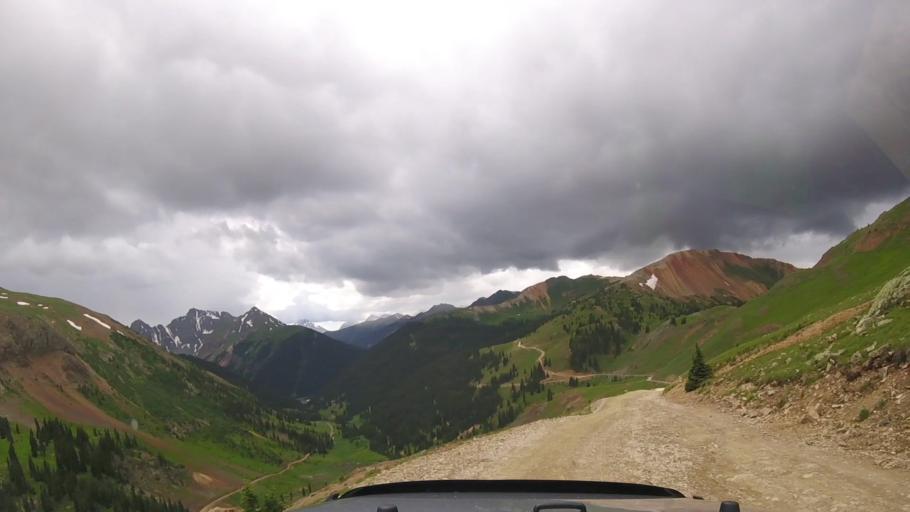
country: US
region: Colorado
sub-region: San Juan County
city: Silverton
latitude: 37.9135
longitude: -107.6379
